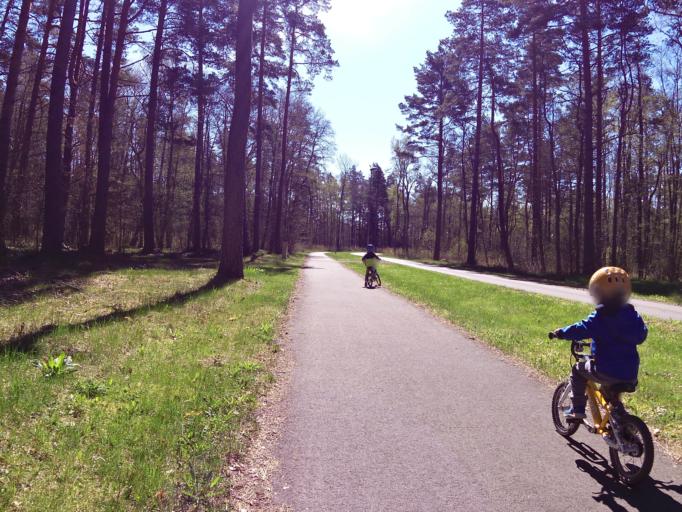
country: EE
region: Harju
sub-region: Raasiku vald
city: Raasiku
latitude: 59.4888
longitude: 25.1727
